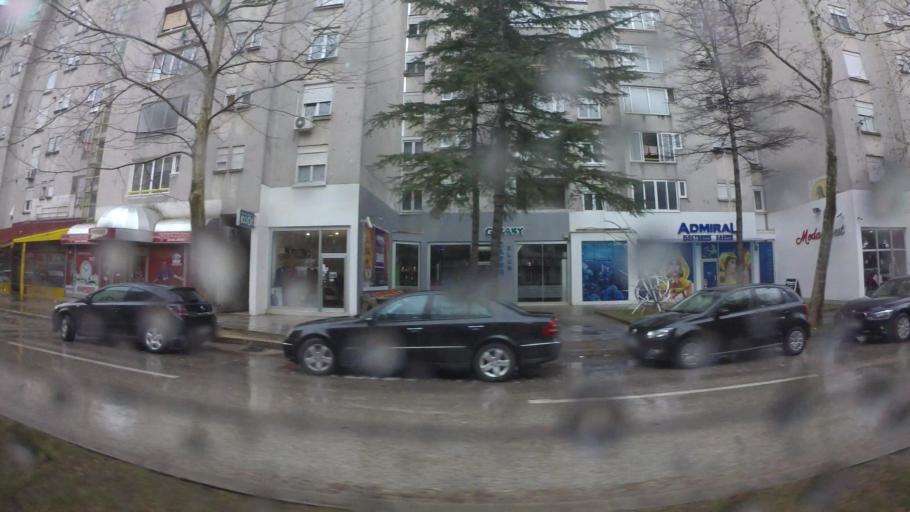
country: BA
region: Federation of Bosnia and Herzegovina
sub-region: Hercegovacko-Bosanski Kanton
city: Mostar
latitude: 43.3480
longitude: 17.8028
